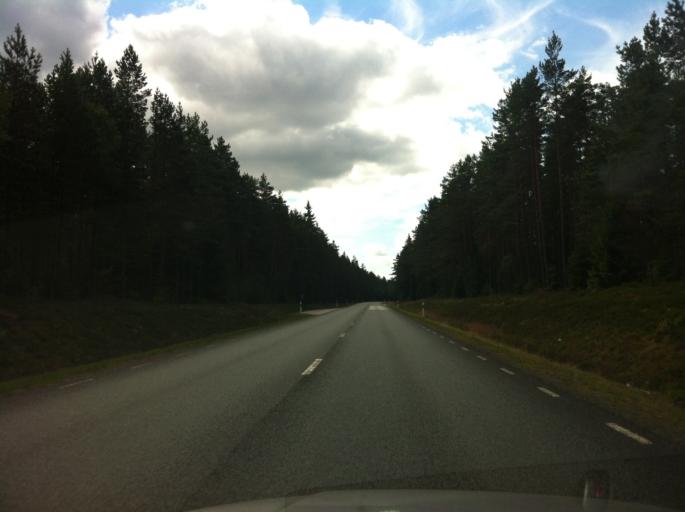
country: SE
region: Joenkoeping
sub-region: Gislaveds Kommun
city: Gislaved
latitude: 57.4108
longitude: 13.6000
